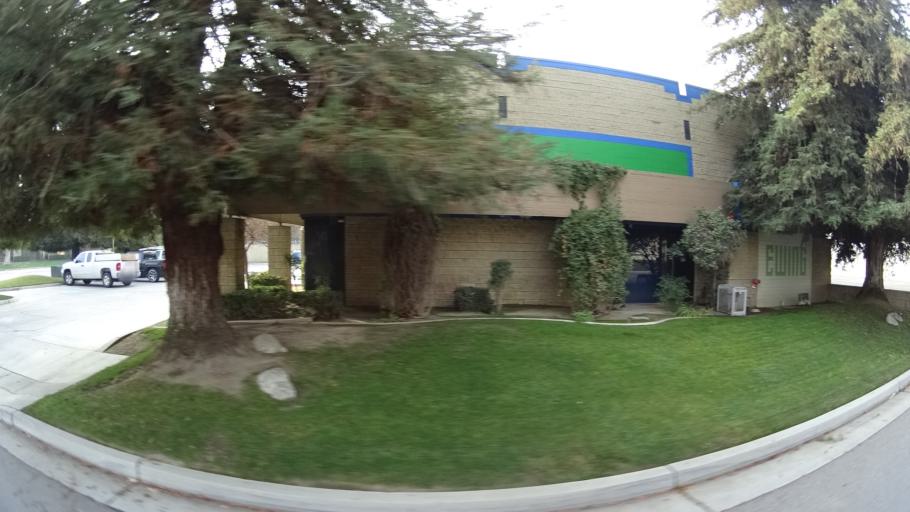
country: US
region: California
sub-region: Kern County
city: Bakersfield
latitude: 35.3894
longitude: -119.0380
